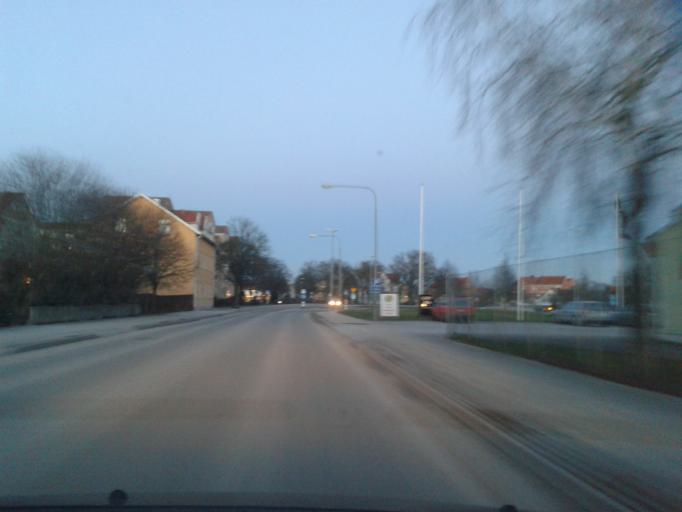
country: SE
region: Gotland
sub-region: Gotland
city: Visby
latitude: 57.6309
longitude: 18.2875
